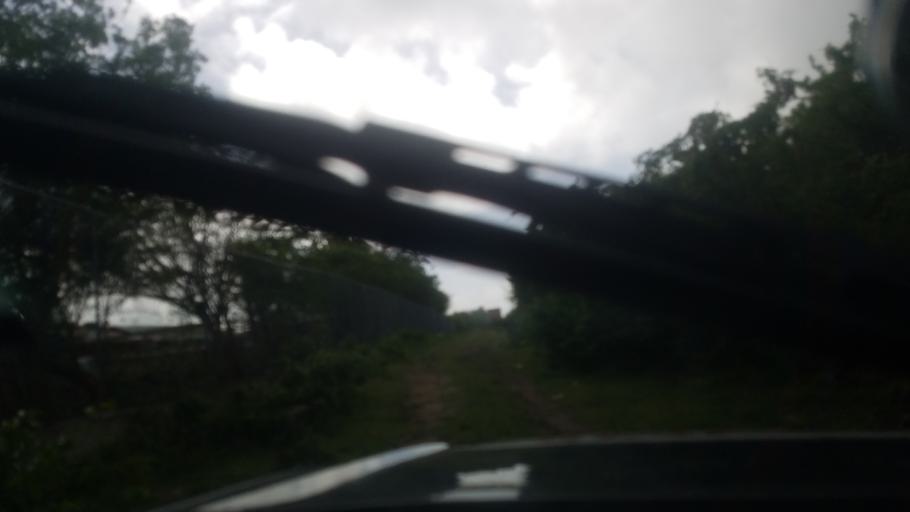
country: LC
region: Laborie Quarter
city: Laborie
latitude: 13.7342
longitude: -60.9775
